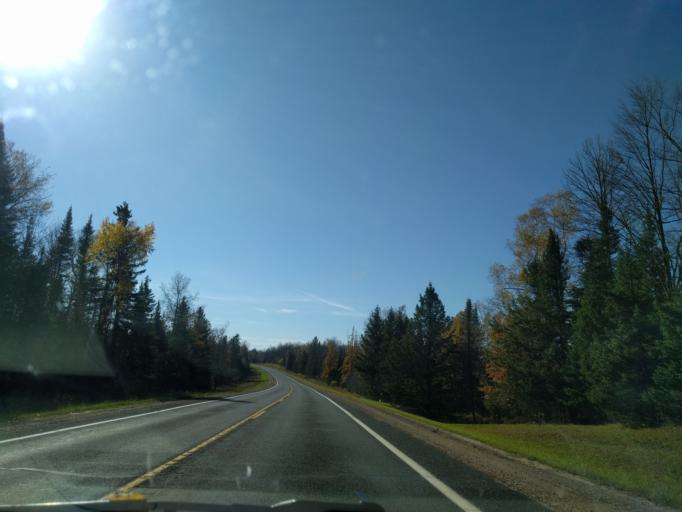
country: US
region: Michigan
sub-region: Iron County
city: Crystal Falls
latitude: 46.1693
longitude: -88.0682
